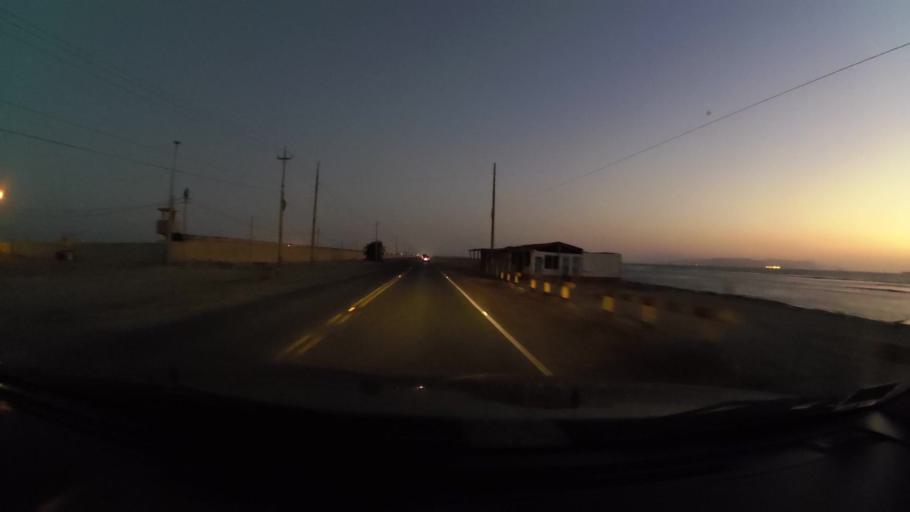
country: PE
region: Ica
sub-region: Provincia de Pisco
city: Pisco
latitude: -13.7479
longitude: -76.2287
